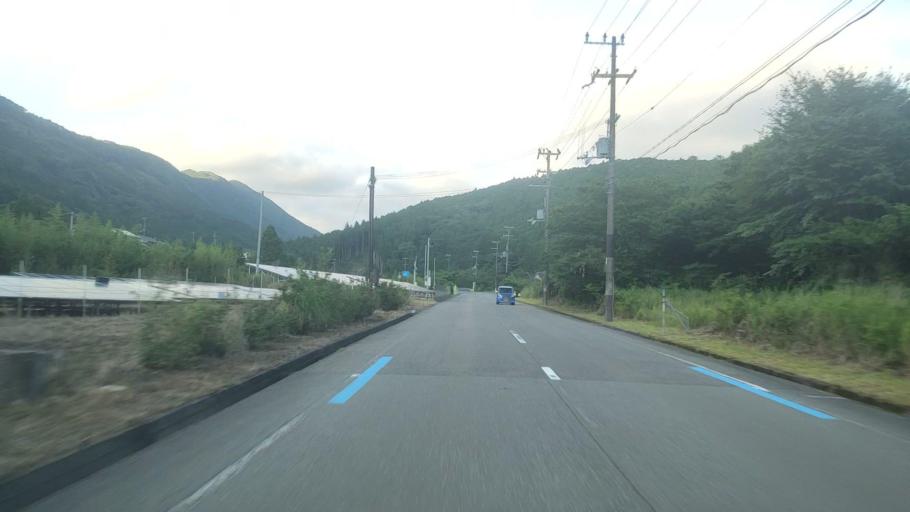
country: JP
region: Wakayama
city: Tanabe
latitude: 33.8212
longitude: 135.6290
